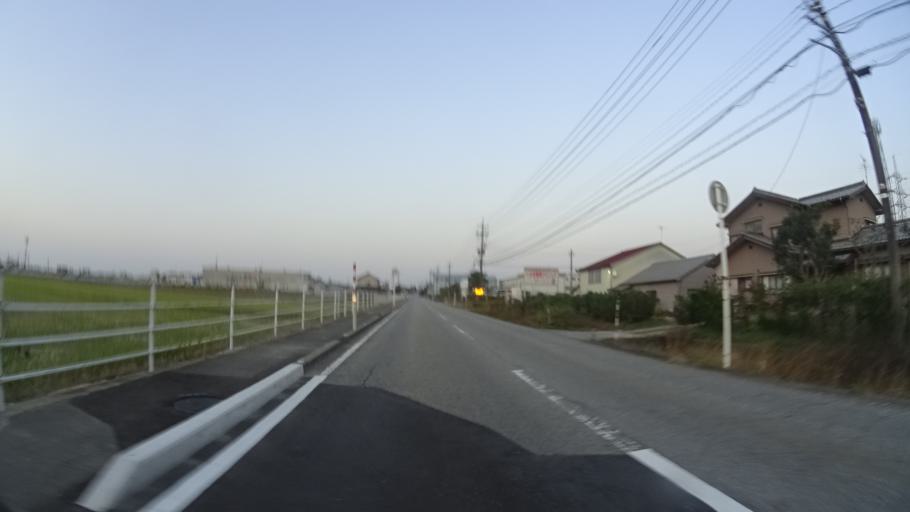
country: JP
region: Toyama
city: Kamiichi
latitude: 36.7359
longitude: 137.3704
